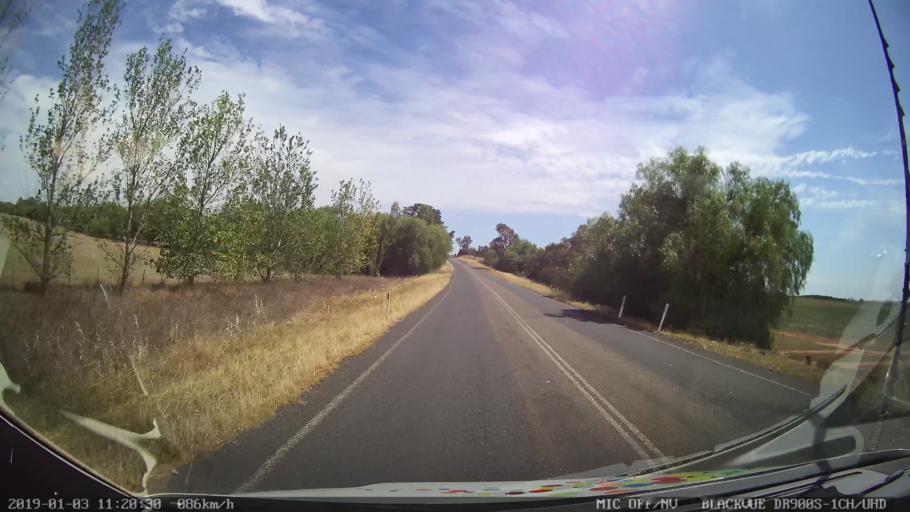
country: AU
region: New South Wales
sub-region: Young
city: Young
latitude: -34.1003
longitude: 148.2547
